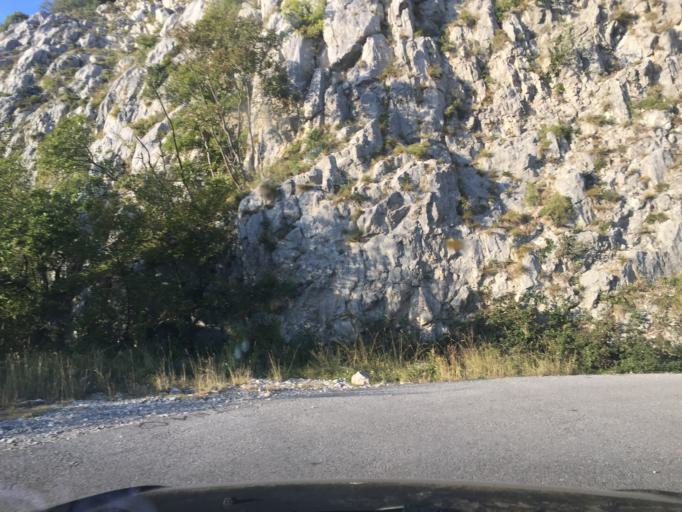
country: SI
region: Vipava
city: Vipava
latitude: 45.8005
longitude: 13.9972
